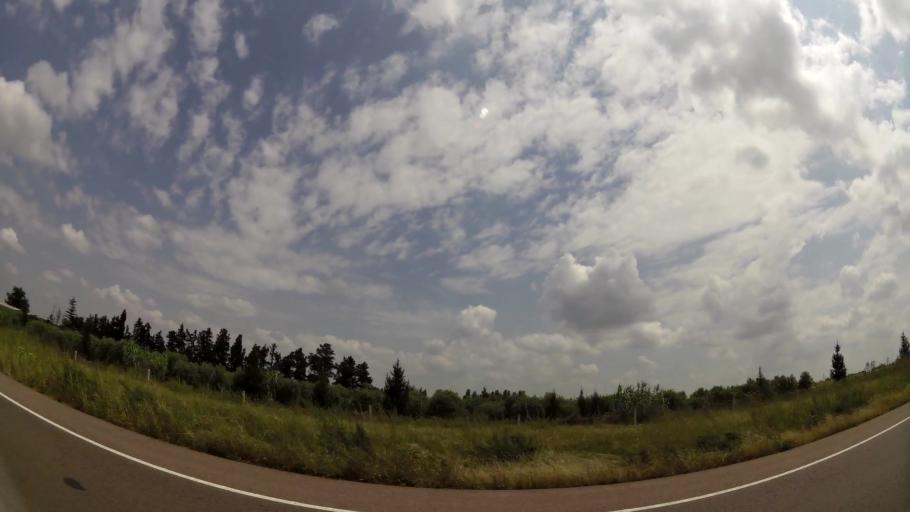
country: MA
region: Rabat-Sale-Zemmour-Zaer
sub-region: Khemisset
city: Tiflet
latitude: 33.9837
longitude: -6.5311
